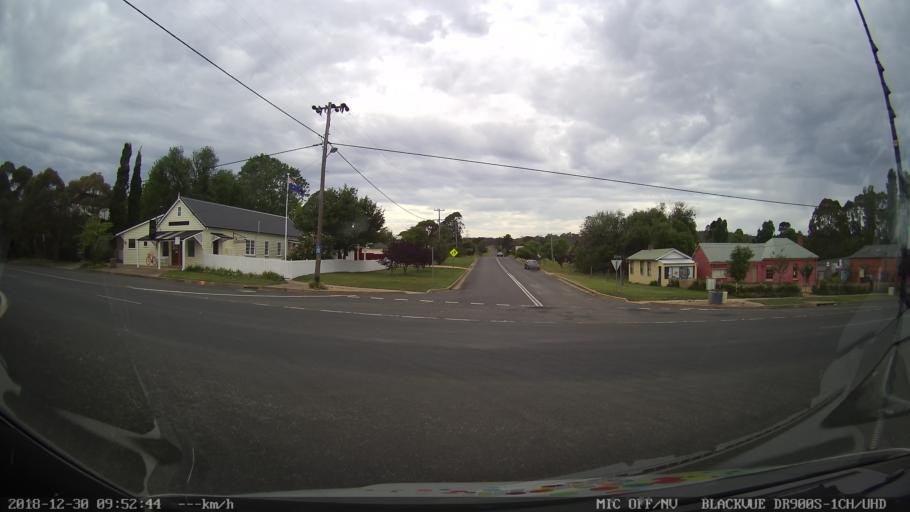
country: AU
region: New South Wales
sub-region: Cooma-Monaro
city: Cooma
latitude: -36.5118
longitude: 149.2846
